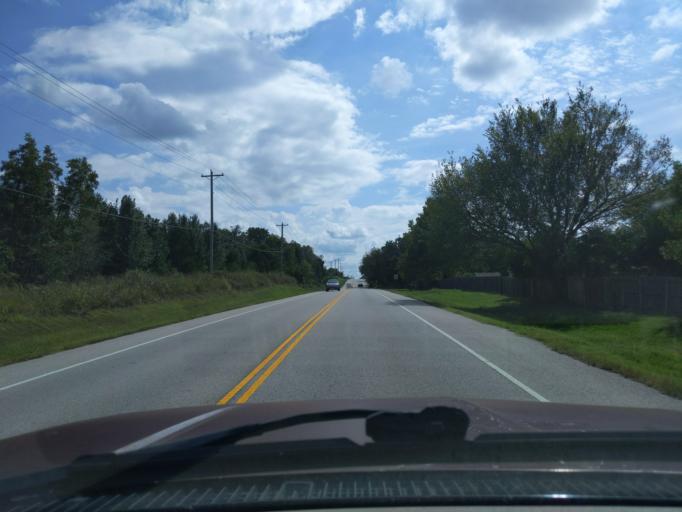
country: US
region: Oklahoma
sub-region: Tulsa County
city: Oakhurst
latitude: 36.0695
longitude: -96.0116
